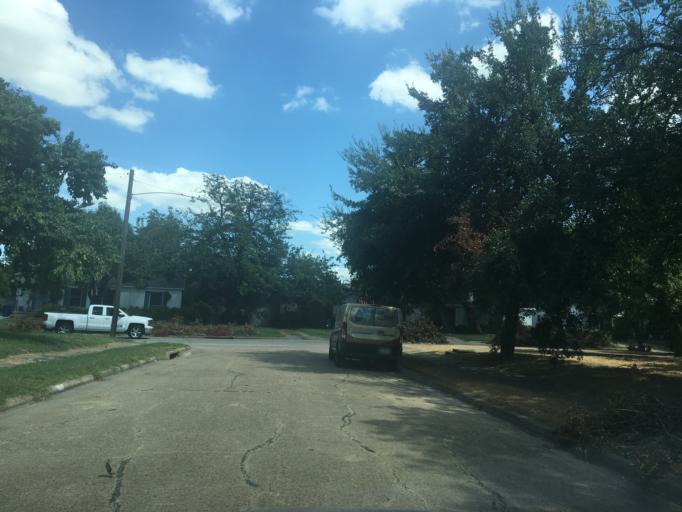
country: US
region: Texas
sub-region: Dallas County
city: Garland
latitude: 32.8391
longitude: -96.6888
